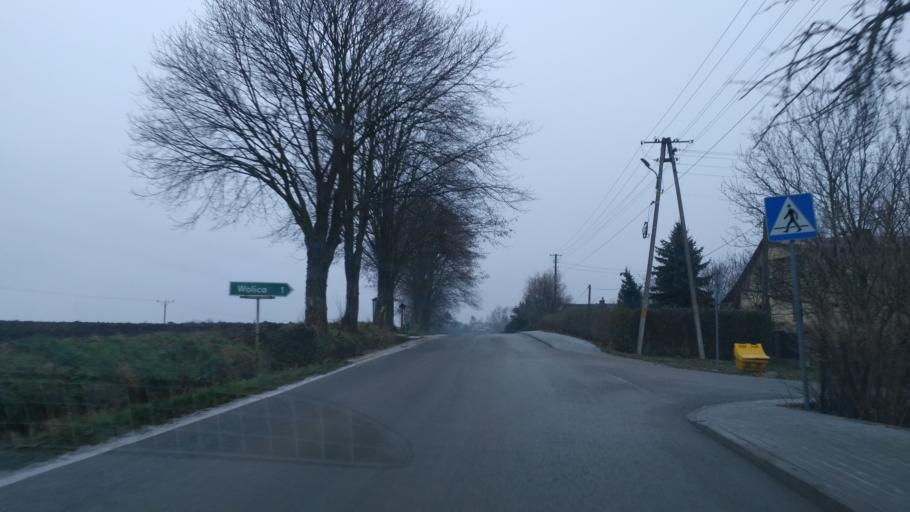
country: PL
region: Subcarpathian Voivodeship
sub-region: Powiat przeworski
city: Kanczuga
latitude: 50.0102
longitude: 22.4273
